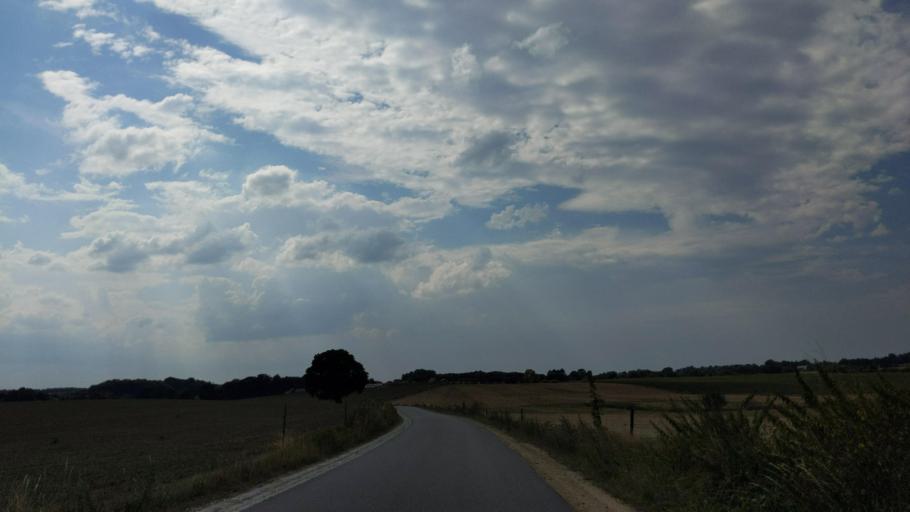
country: DE
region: Mecklenburg-Vorpommern
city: Selmsdorf
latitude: 53.8384
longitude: 10.8788
